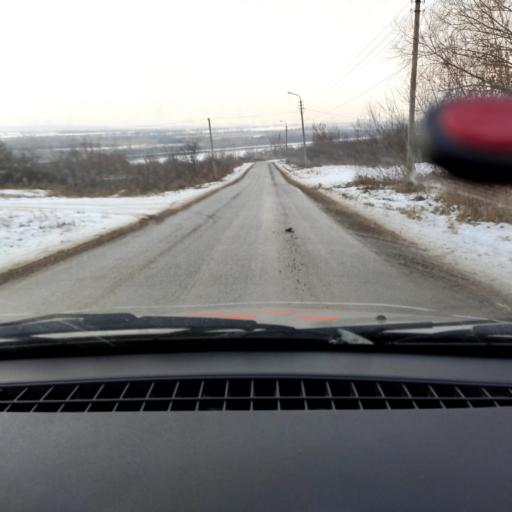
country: RU
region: Bashkortostan
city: Blagoveshchensk
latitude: 54.8901
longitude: 56.0466
